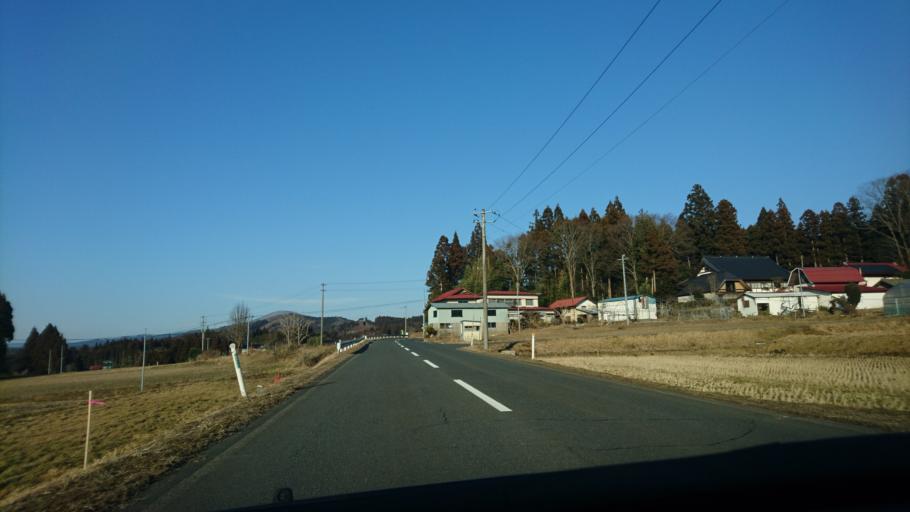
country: JP
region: Iwate
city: Ichinoseki
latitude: 38.8877
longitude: 141.3959
